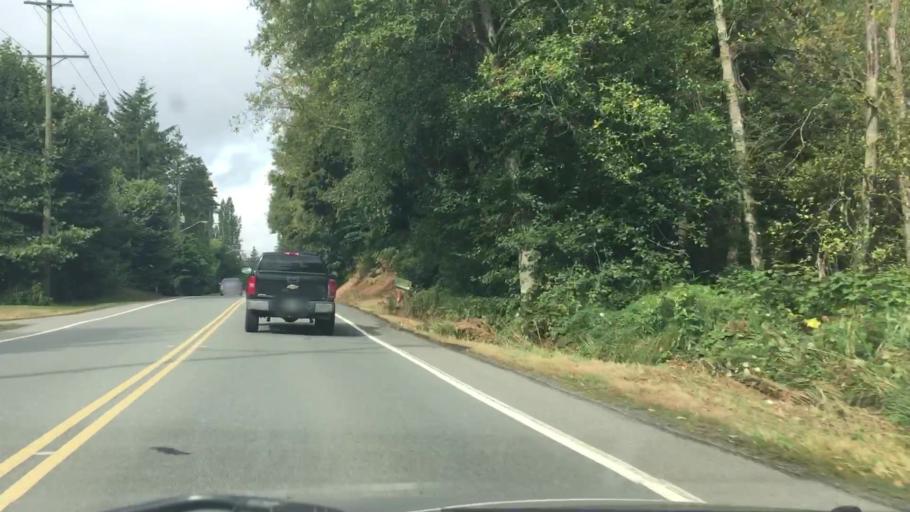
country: CA
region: British Columbia
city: Langley
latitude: 49.1040
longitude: -122.5752
